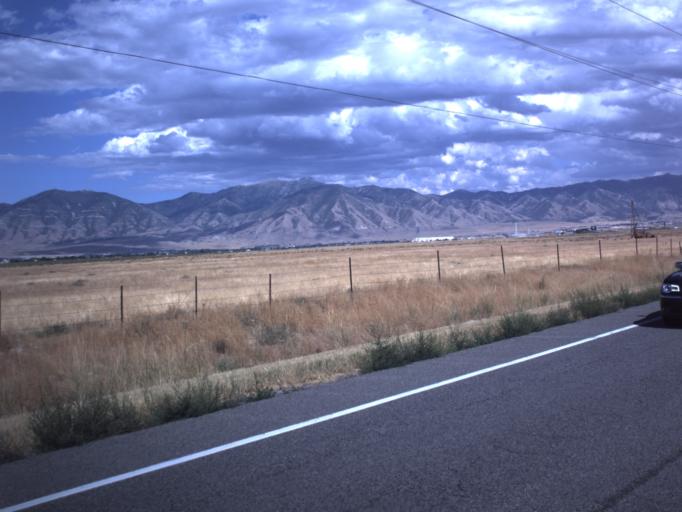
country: US
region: Utah
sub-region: Tooele County
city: Grantsville
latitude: 40.5865
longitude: -112.4118
